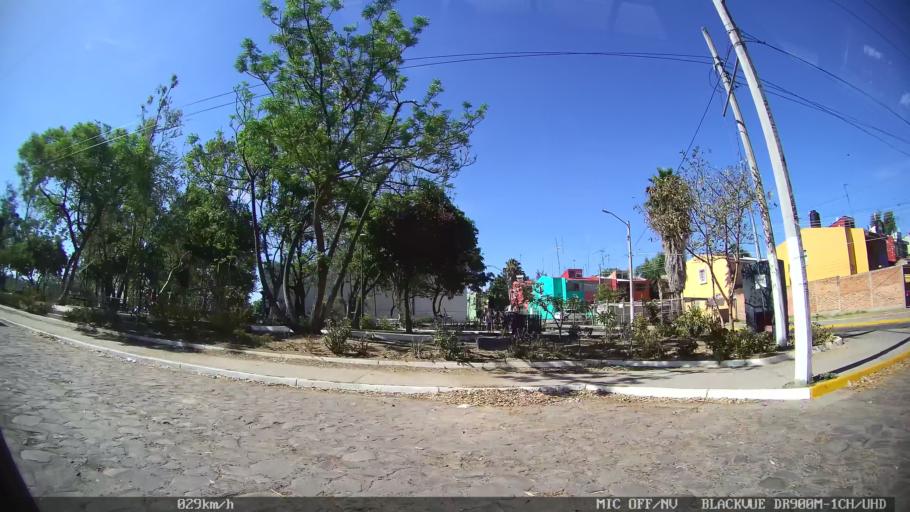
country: MX
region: Jalisco
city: Tlaquepaque
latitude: 20.6829
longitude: -103.2705
